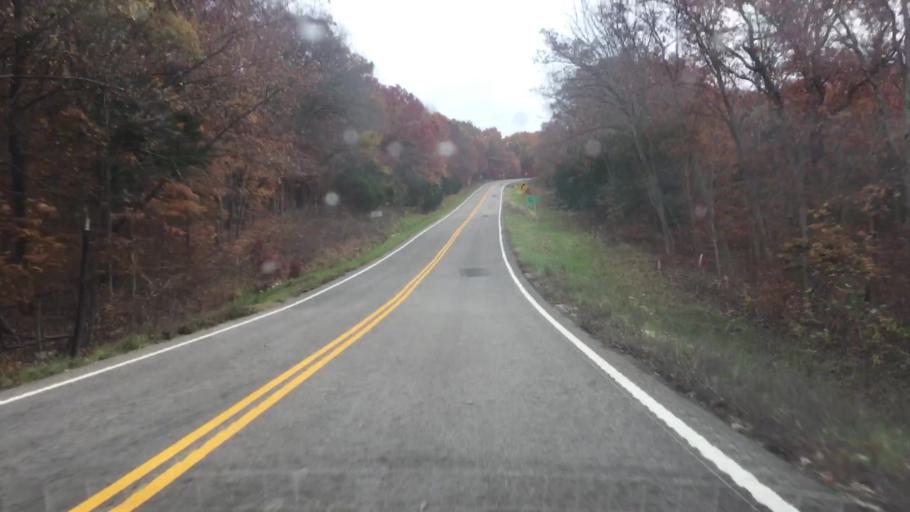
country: US
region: Missouri
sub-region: Gasconade County
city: Hermann
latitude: 38.7197
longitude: -91.6471
